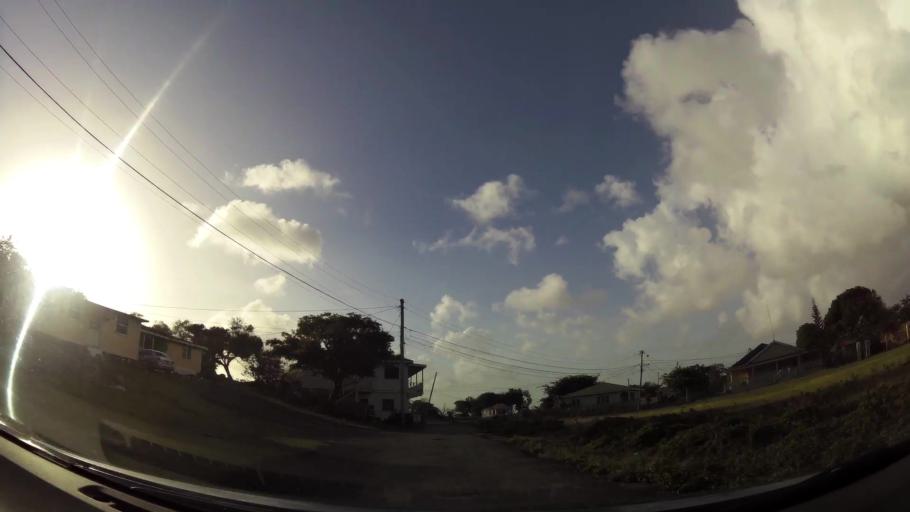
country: KN
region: Saint John Figtree
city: Fig Tree
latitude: 17.1165
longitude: -62.6044
